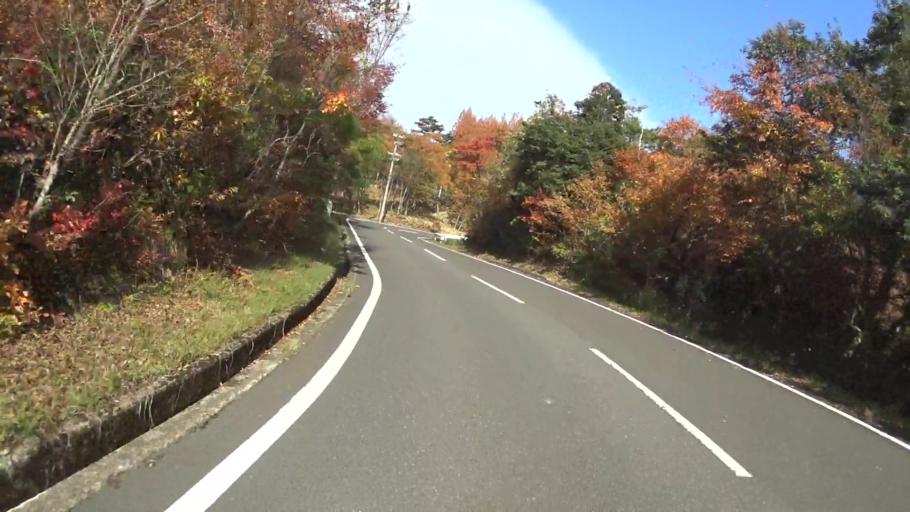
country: JP
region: Kyoto
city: Maizuru
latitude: 35.5319
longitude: 135.3942
